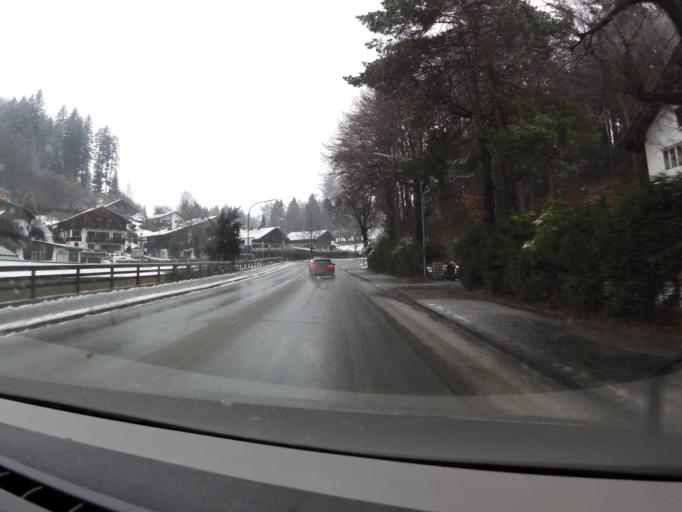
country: DE
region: Bavaria
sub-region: Upper Bavaria
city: Bad Wiessee
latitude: 47.7213
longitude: 11.7170
